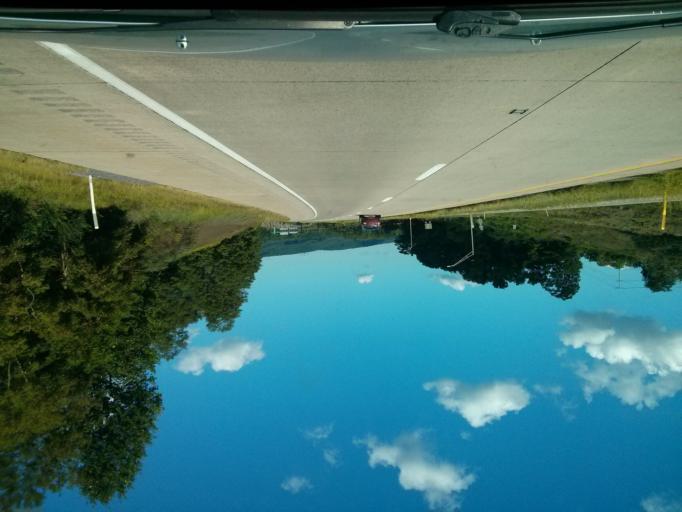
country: US
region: Pennsylvania
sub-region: Centre County
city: Park Forest Village
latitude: 40.8156
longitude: -77.9282
